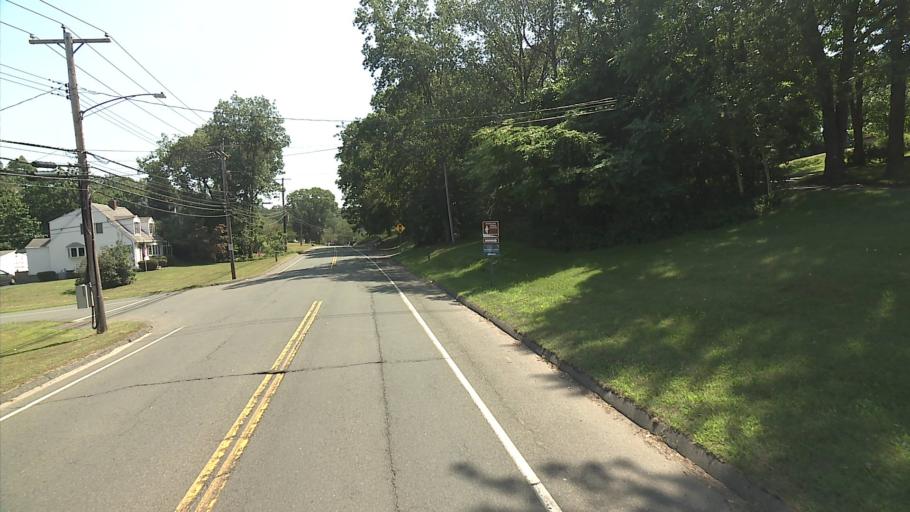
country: US
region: Connecticut
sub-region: New Haven County
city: East Haven
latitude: 41.2617
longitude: -72.8643
